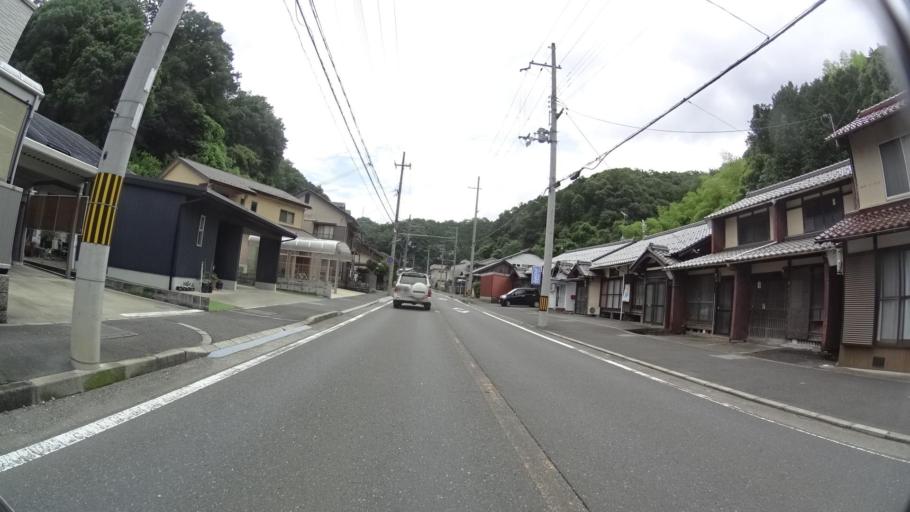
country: JP
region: Kyoto
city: Maizuru
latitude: 35.4673
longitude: 135.3654
